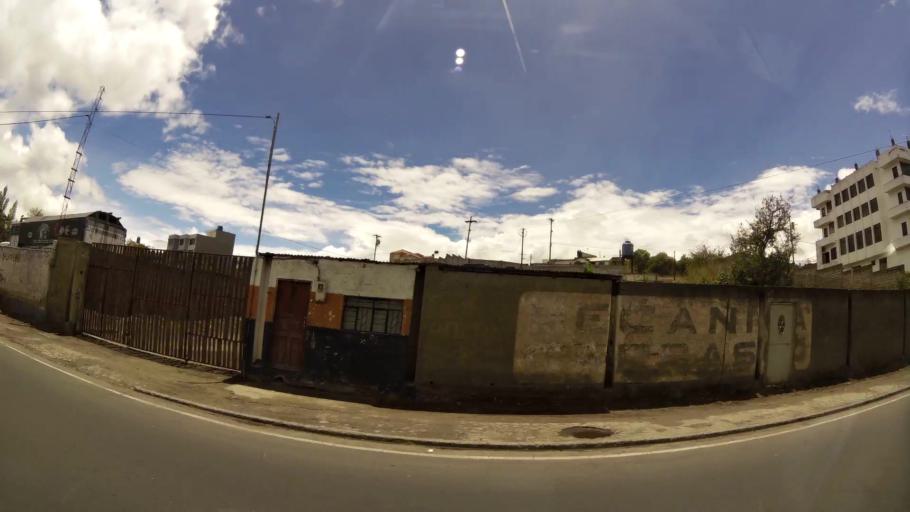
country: EC
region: Tungurahua
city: Pelileo
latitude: -1.3259
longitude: -78.5467
